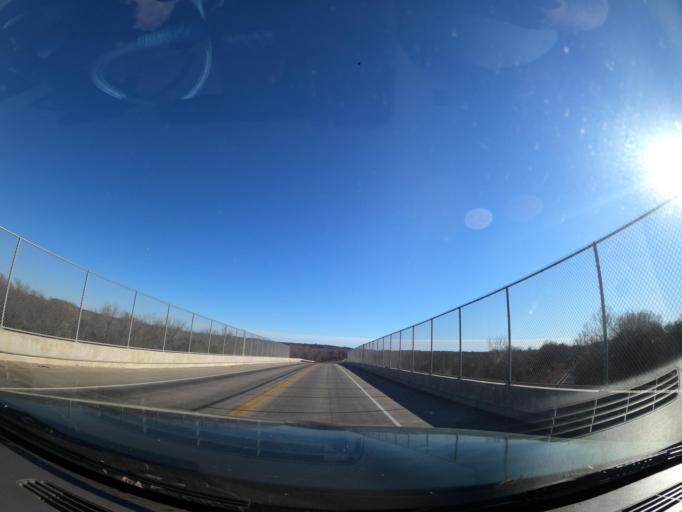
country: US
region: Oklahoma
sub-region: McIntosh County
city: Eufaula
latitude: 35.2688
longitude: -95.5840
